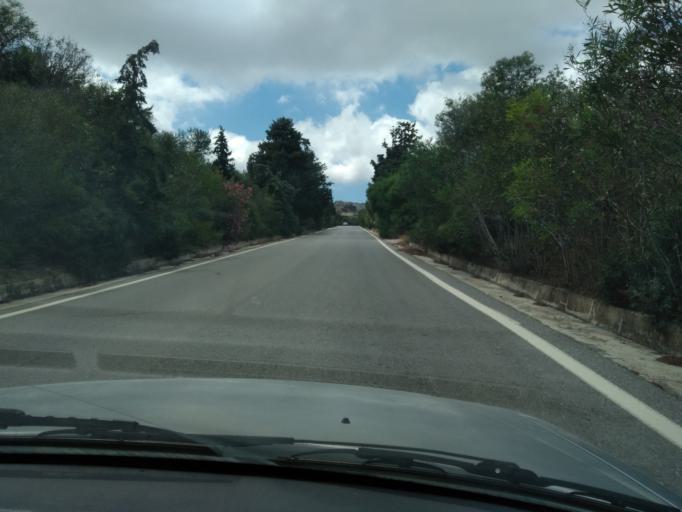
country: GR
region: Crete
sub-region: Nomos Lasithiou
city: Makry-Gialos
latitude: 35.0688
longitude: 26.0470
